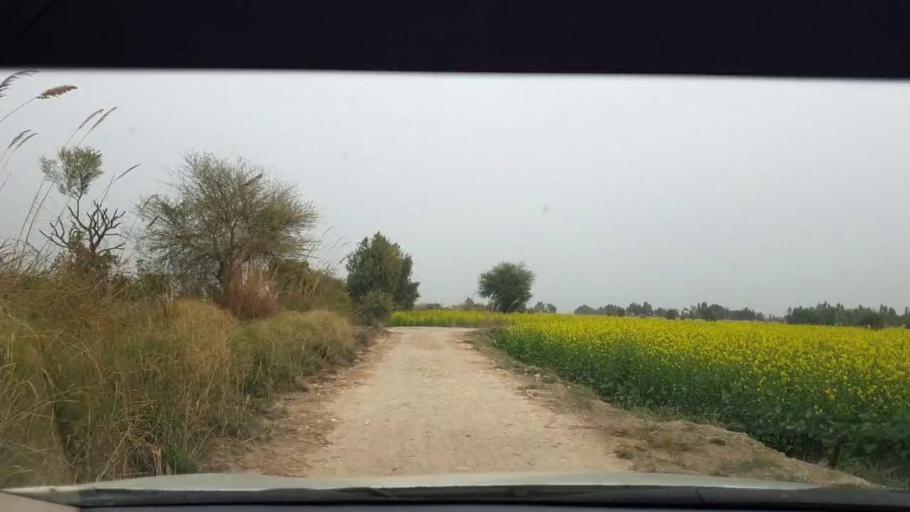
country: PK
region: Sindh
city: Jhol
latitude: 25.9245
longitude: 68.8539
